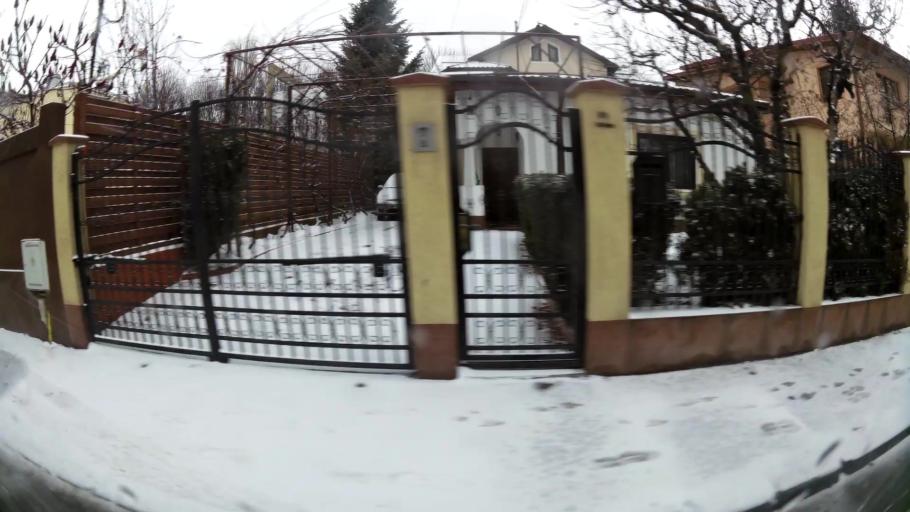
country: RO
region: Prahova
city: Ploiesti
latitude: 44.9300
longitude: 26.0154
